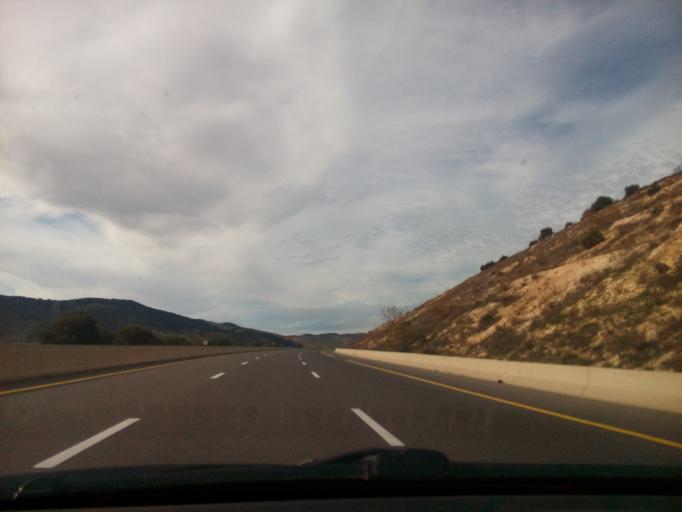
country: DZ
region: Sidi Bel Abbes
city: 'Ain el Berd
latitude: 35.4124
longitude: -0.4827
